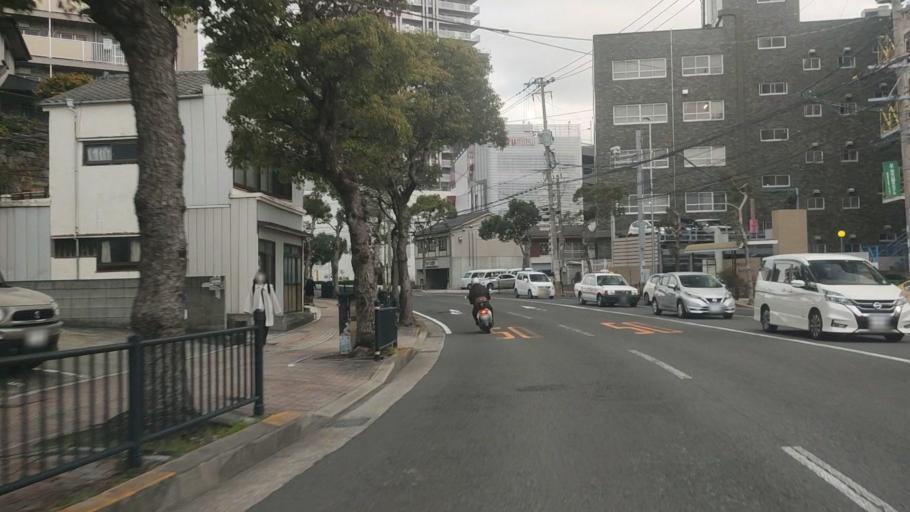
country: JP
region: Nagasaki
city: Nagasaki-shi
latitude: 32.7487
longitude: 129.8645
